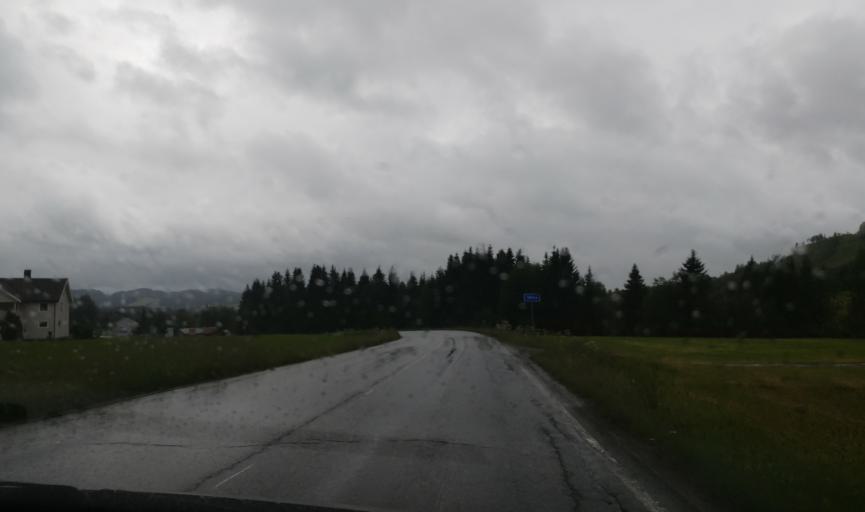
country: NO
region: Sor-Trondelag
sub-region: Selbu
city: Mebonden
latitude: 63.2892
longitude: 11.0716
